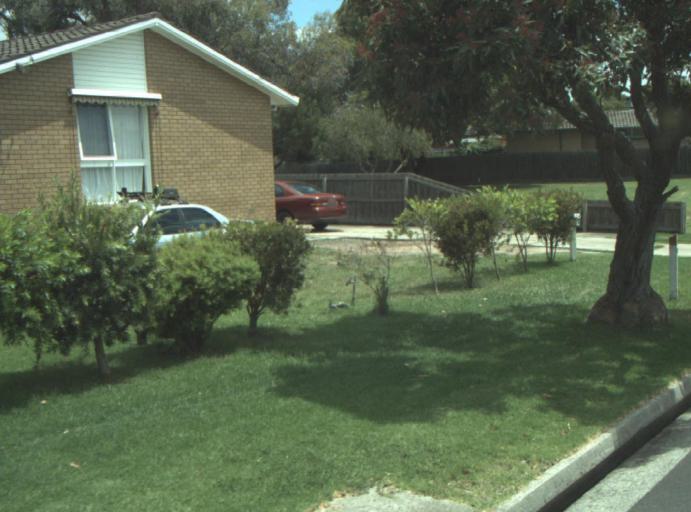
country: AU
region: Victoria
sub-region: Greater Geelong
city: Wandana Heights
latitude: -38.1842
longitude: 144.3201
